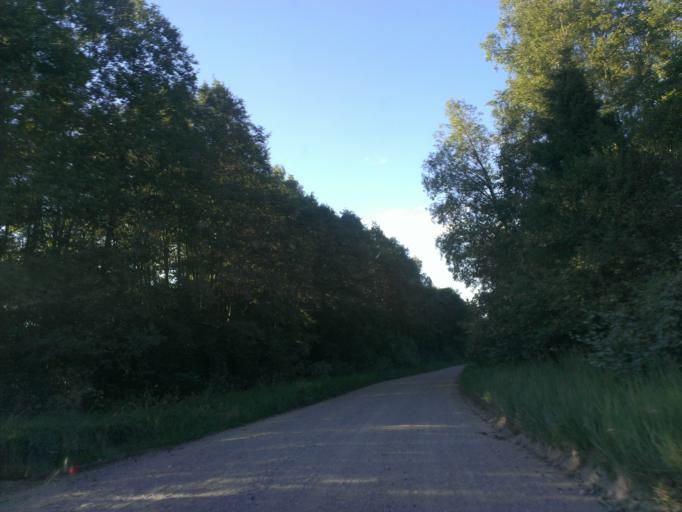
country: LV
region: Malpils
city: Malpils
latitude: 57.0885
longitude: 25.0497
